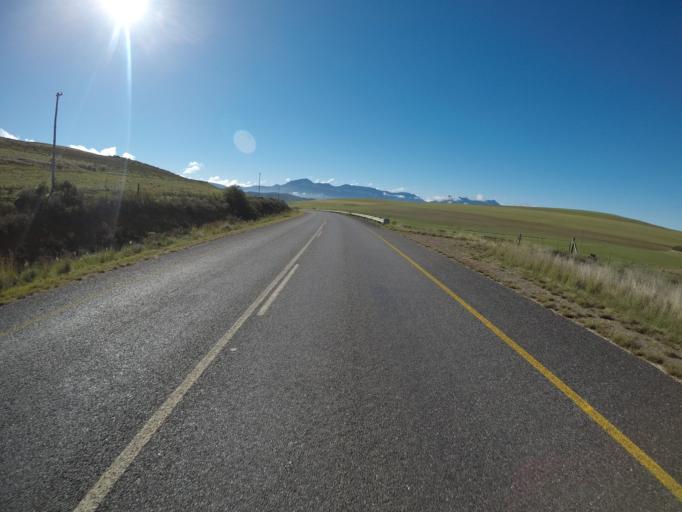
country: ZA
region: Western Cape
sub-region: Overberg District Municipality
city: Caledon
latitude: -34.1323
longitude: 19.5120
